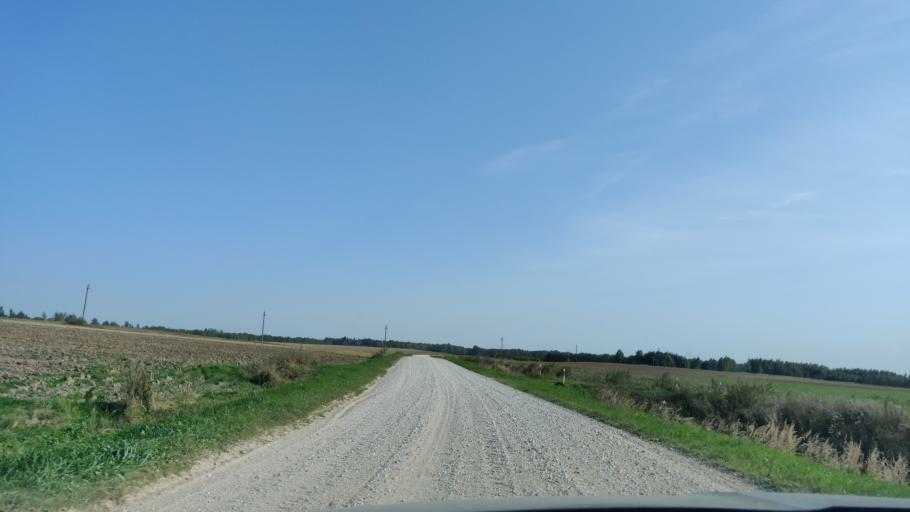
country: LT
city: Sirvintos
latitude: 54.9683
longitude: 24.8435
